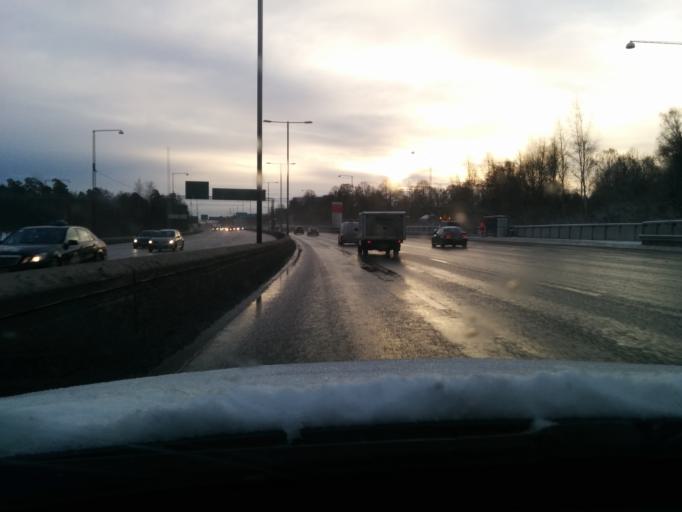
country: SE
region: Stockholm
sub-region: Norrtalje Kommun
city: Bergshamra
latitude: 59.3598
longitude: 18.0282
